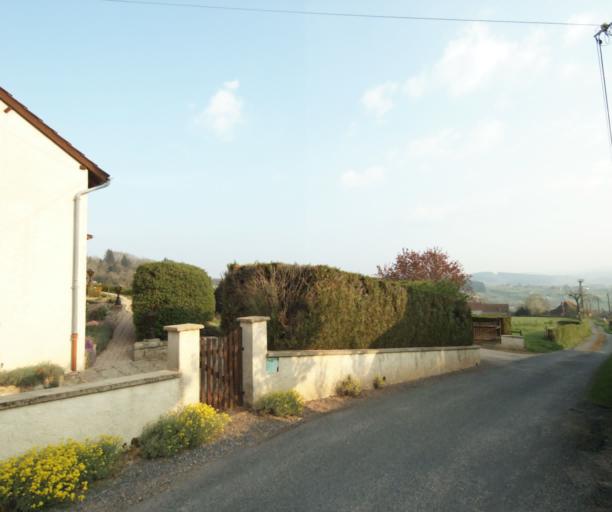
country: FR
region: Bourgogne
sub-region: Departement de Saone-et-Loire
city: Matour
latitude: 46.4339
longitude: 4.4602
